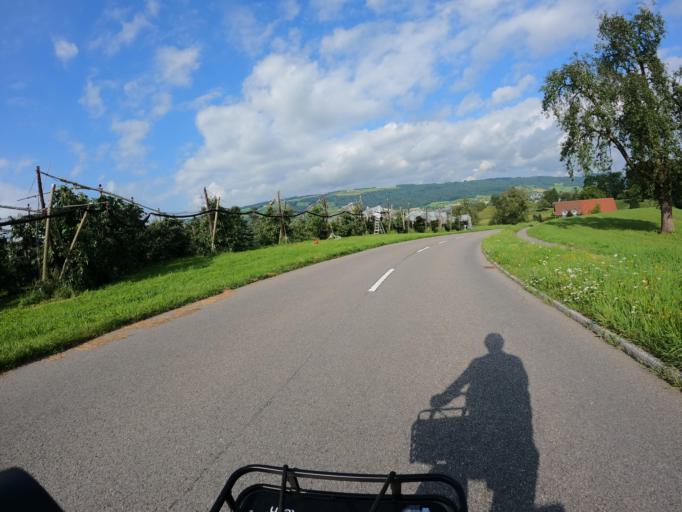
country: CH
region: Lucerne
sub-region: Hochdorf District
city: Hitzkirch
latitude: 47.2154
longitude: 8.2717
